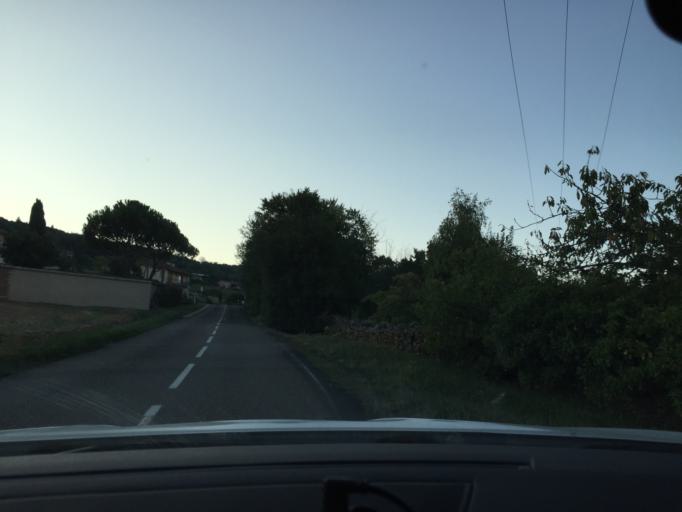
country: FR
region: Rhone-Alpes
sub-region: Departement du Rhone
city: Charnay
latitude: 45.8996
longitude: 4.6571
